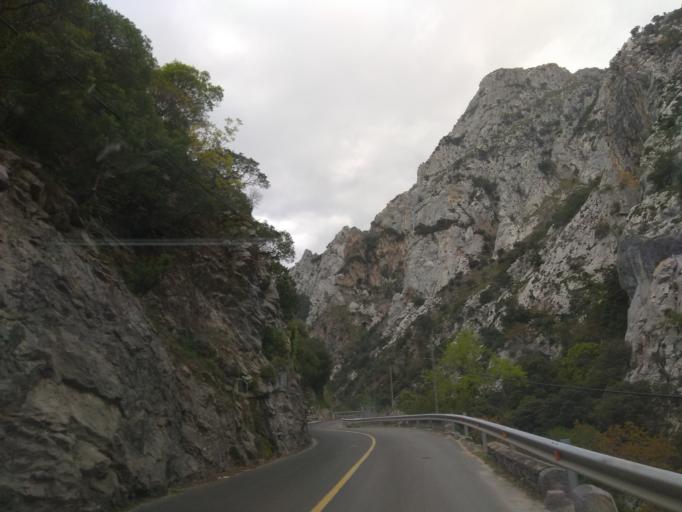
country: ES
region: Cantabria
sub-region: Provincia de Cantabria
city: Potes
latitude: 43.2084
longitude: -4.5944
